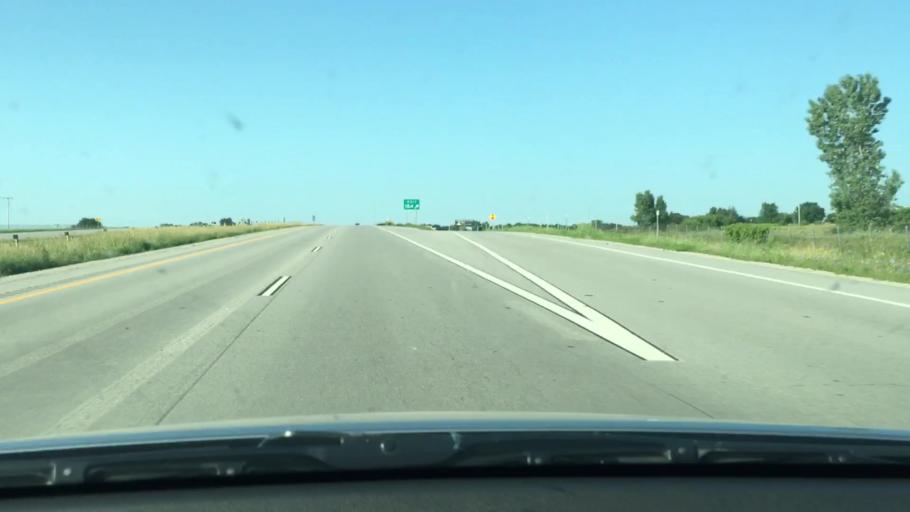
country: US
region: Wisconsin
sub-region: Brown County
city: Wrightstown
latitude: 44.3529
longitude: -88.1904
